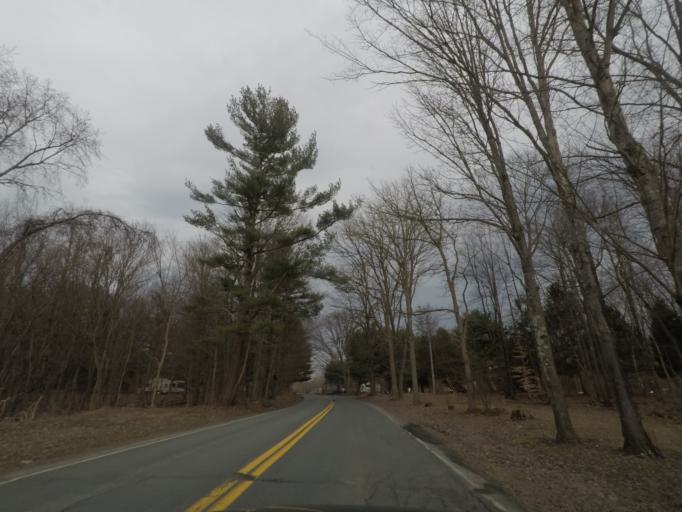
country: US
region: New York
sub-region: Saratoga County
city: Stillwater
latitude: 42.9225
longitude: -73.5183
